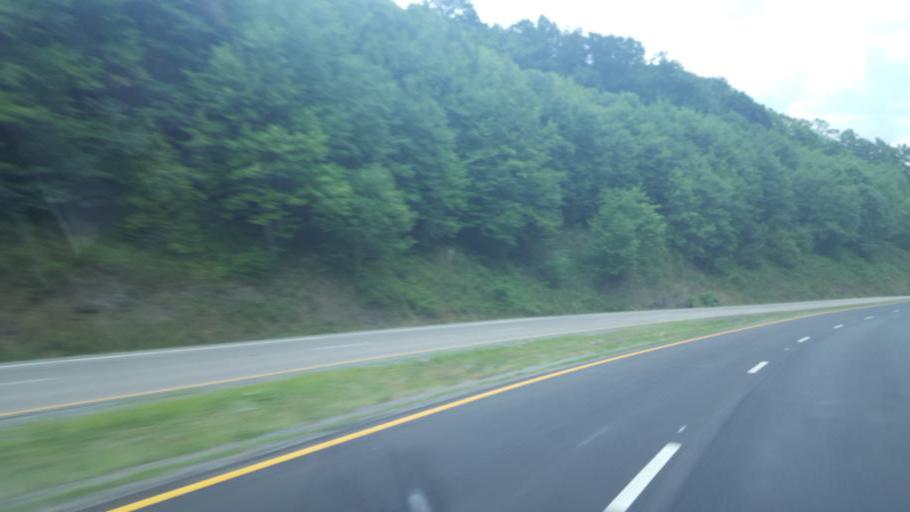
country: US
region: Kentucky
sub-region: Letcher County
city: Jenkins
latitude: 37.1539
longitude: -82.6159
